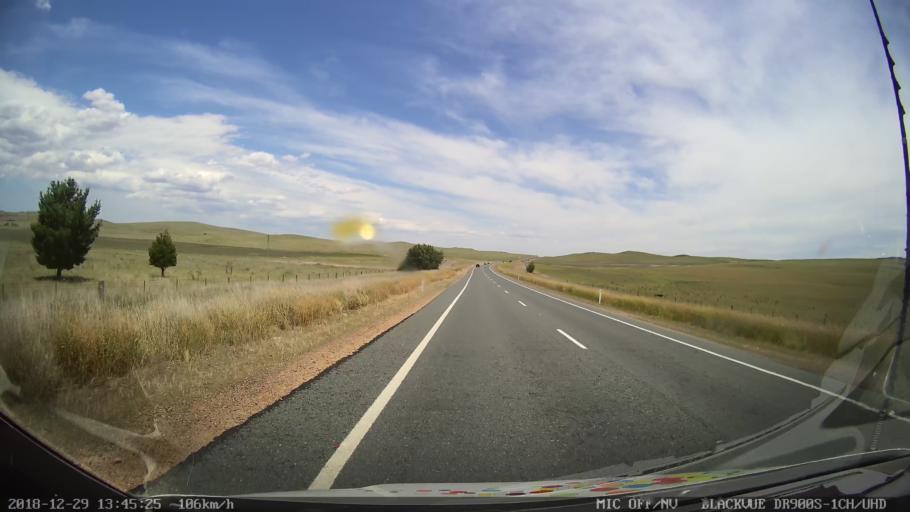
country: AU
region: New South Wales
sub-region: Cooma-Monaro
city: Cooma
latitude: -36.0964
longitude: 149.1454
